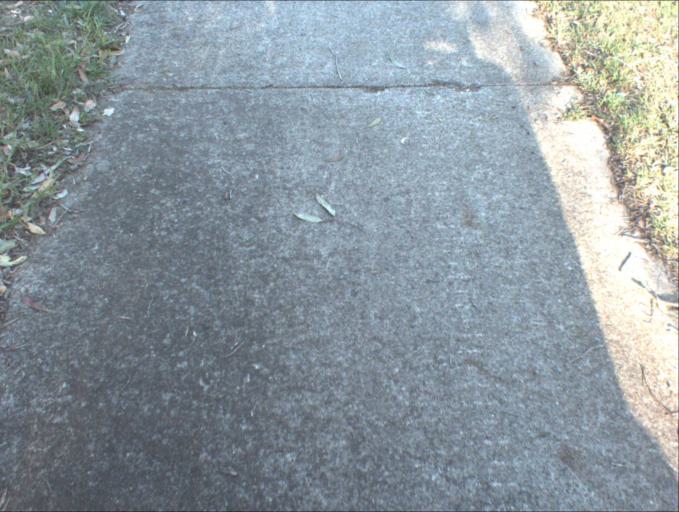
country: AU
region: Queensland
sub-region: Logan
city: Chambers Flat
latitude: -27.7679
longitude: 153.1229
